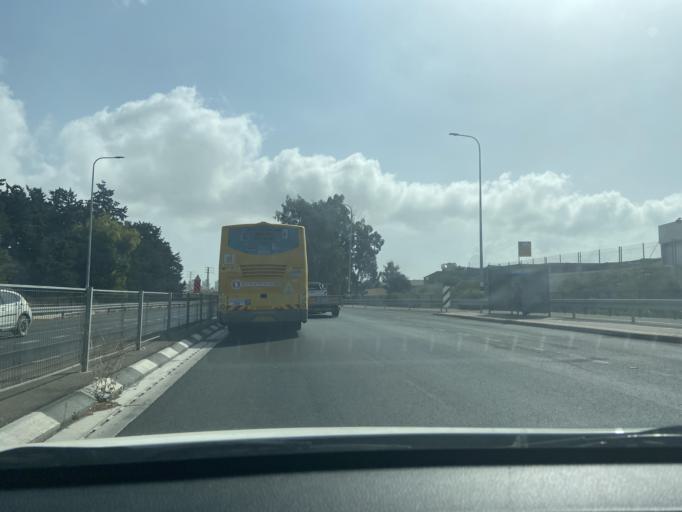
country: IL
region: Northern District
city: Nahariya
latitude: 33.0331
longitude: 35.1043
